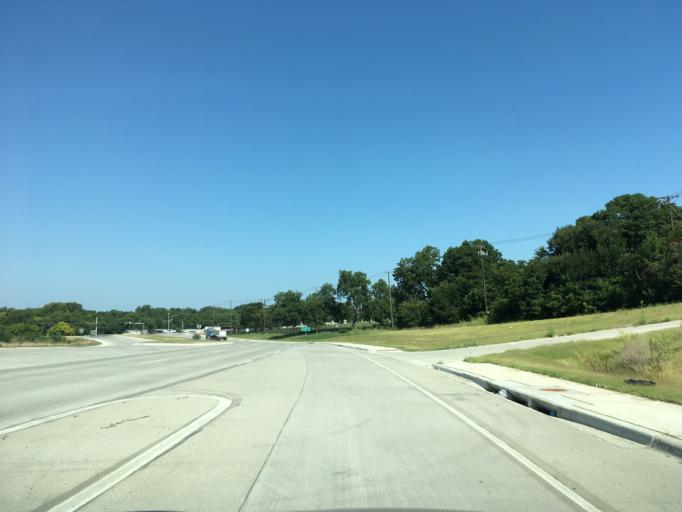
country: US
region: Texas
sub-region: Collin County
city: McKinney
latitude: 33.1754
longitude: -96.6169
